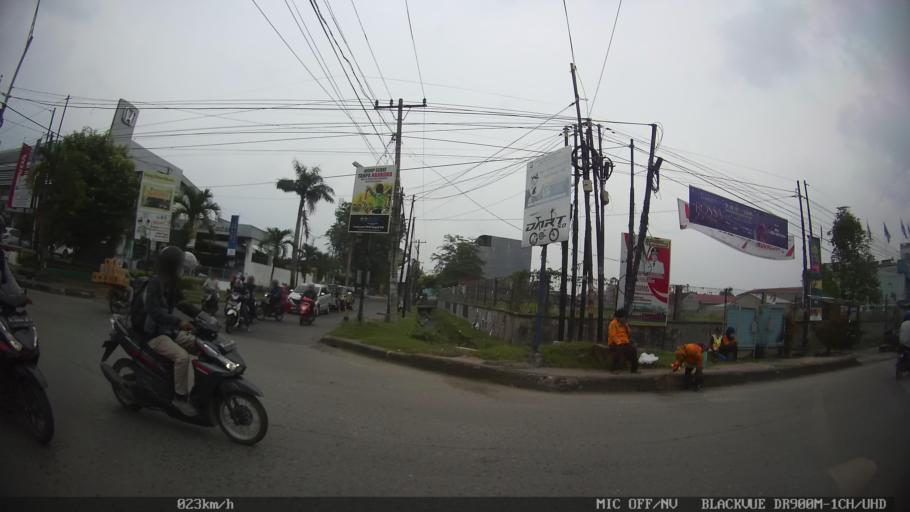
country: ID
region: North Sumatra
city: Deli Tua
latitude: 3.5456
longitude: 98.6980
